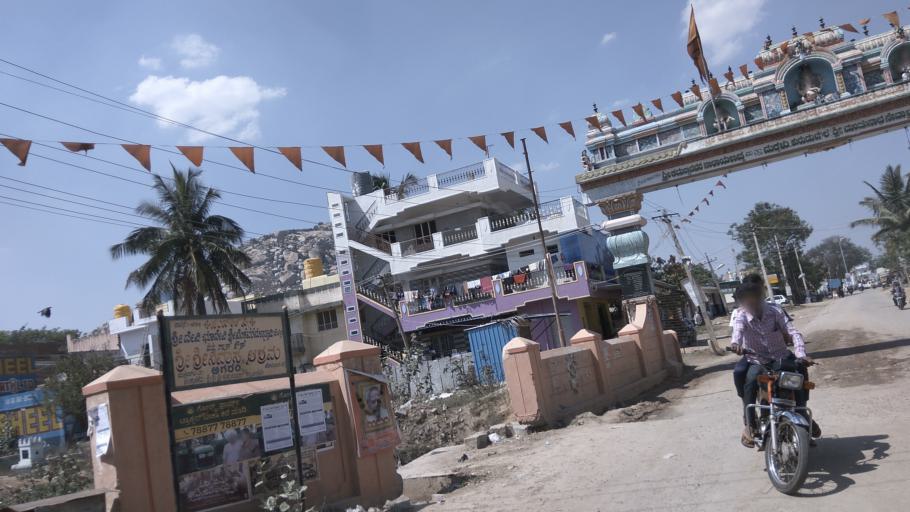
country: IN
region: Karnataka
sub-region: Kolar
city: Mulbagal
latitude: 13.1608
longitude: 78.3847
